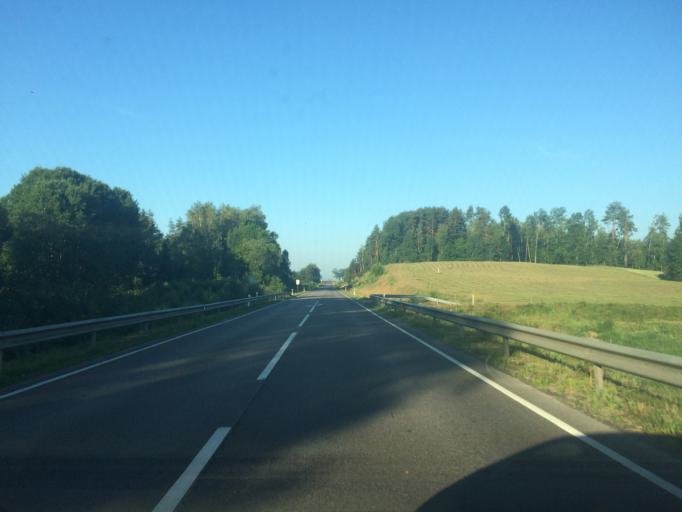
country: LT
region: Utenos apskritis
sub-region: Anyksciai
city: Anyksciai
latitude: 55.4098
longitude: 25.1970
